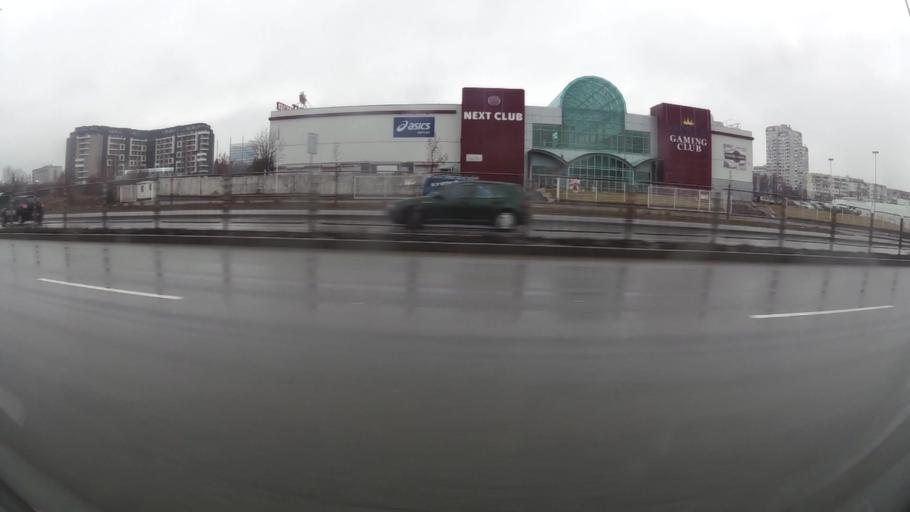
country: BG
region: Sofia-Capital
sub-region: Stolichna Obshtina
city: Sofia
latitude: 42.6365
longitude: 23.3731
